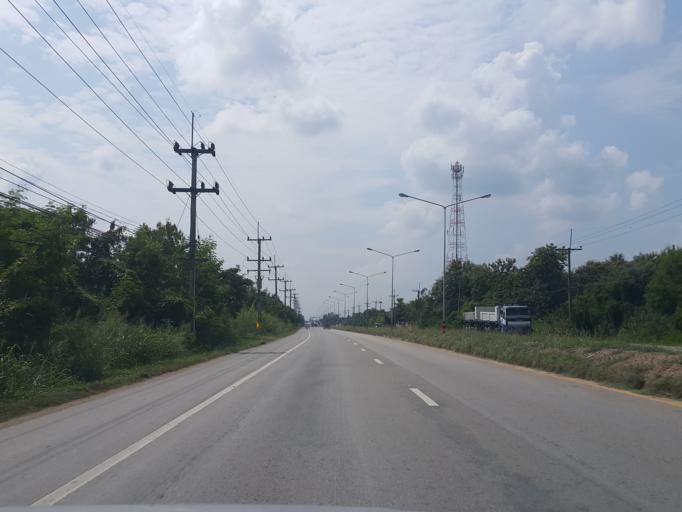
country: TH
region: Chiang Mai
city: Doi Lo
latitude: 18.4978
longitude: 98.8179
